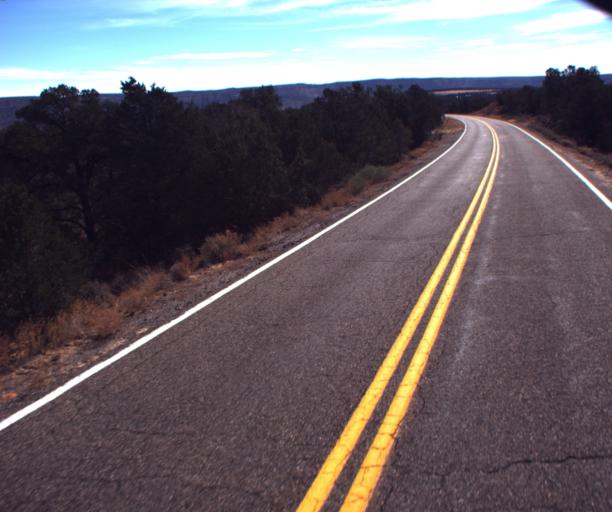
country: US
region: Arizona
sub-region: Navajo County
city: Kayenta
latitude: 36.6221
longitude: -110.5085
